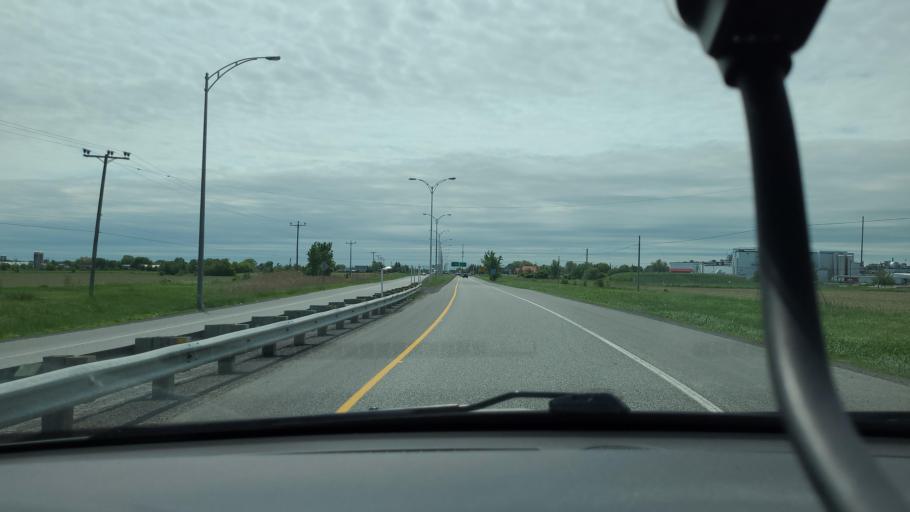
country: CA
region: Quebec
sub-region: Lanaudiere
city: Sainte-Julienne
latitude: 45.9096
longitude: -73.6581
